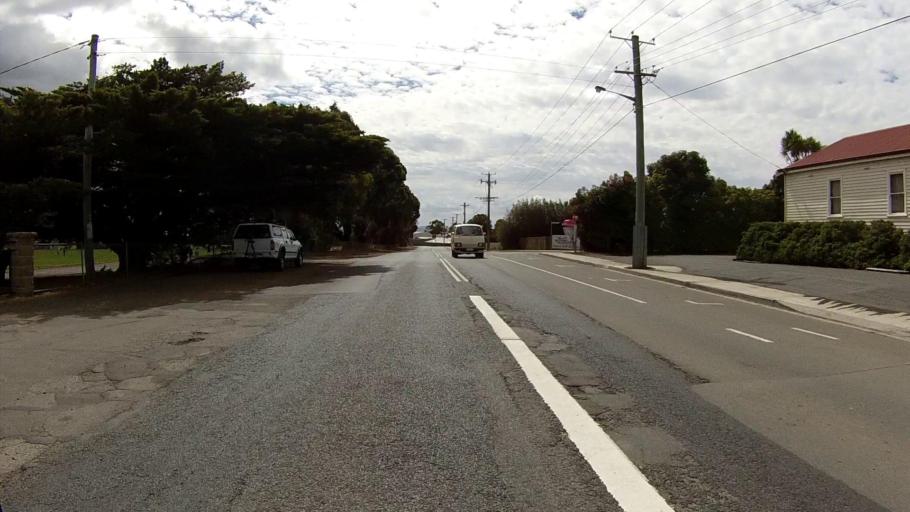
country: AU
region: Tasmania
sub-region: Clarence
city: Cambridge
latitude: -42.8366
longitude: 147.4429
